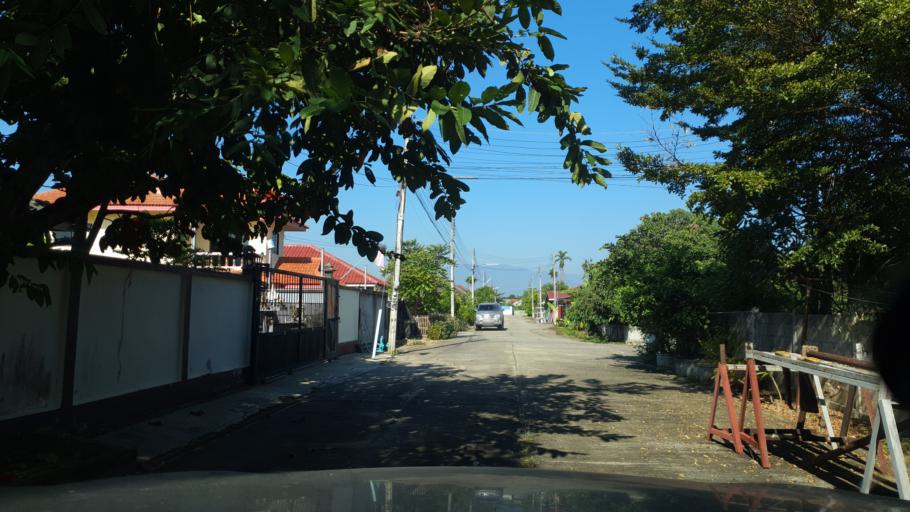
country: TH
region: Chiang Mai
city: Saraphi
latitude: 18.7244
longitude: 99.0604
